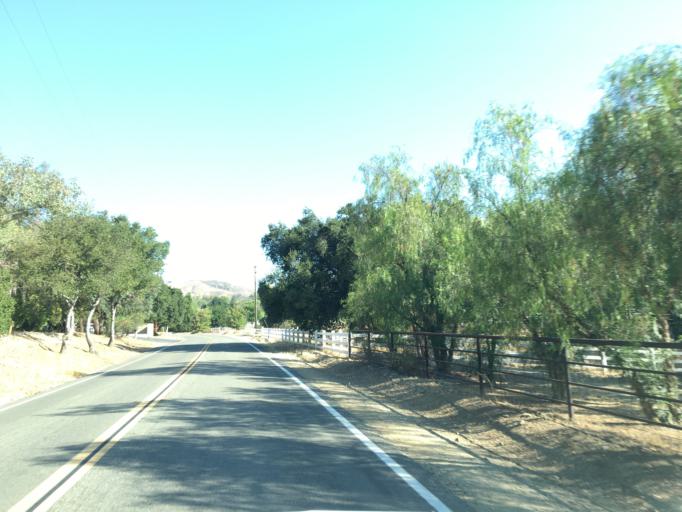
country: US
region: California
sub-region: Los Angeles County
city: Val Verde
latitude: 34.4714
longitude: -118.6701
